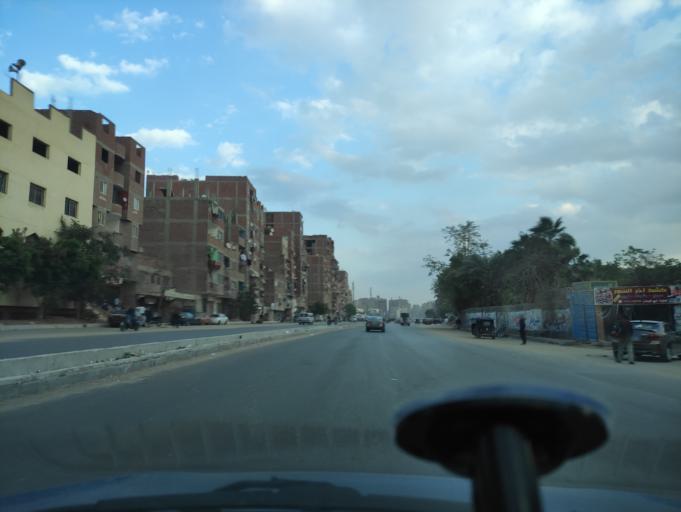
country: EG
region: Muhafazat al Qalyubiyah
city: Al Khankah
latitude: 30.1377
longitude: 31.3484
